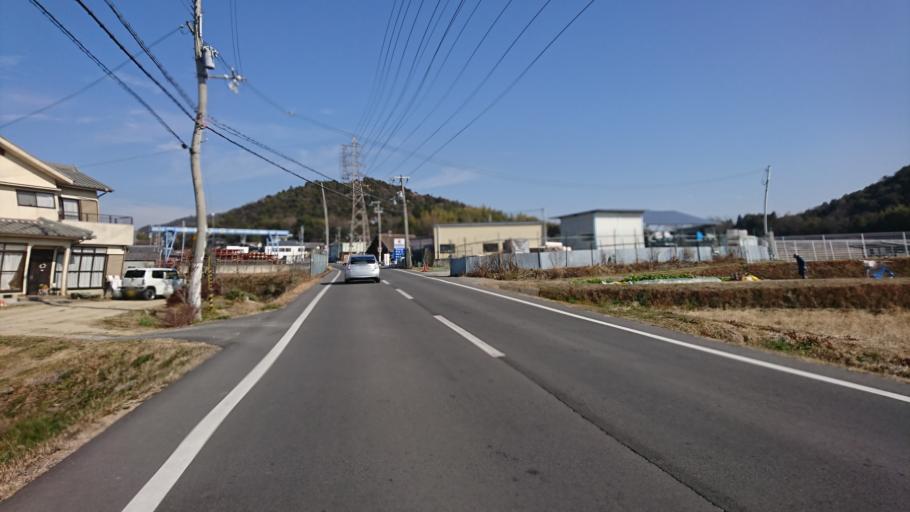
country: JP
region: Hyogo
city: Kakogawacho-honmachi
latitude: 34.7937
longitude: 134.8378
